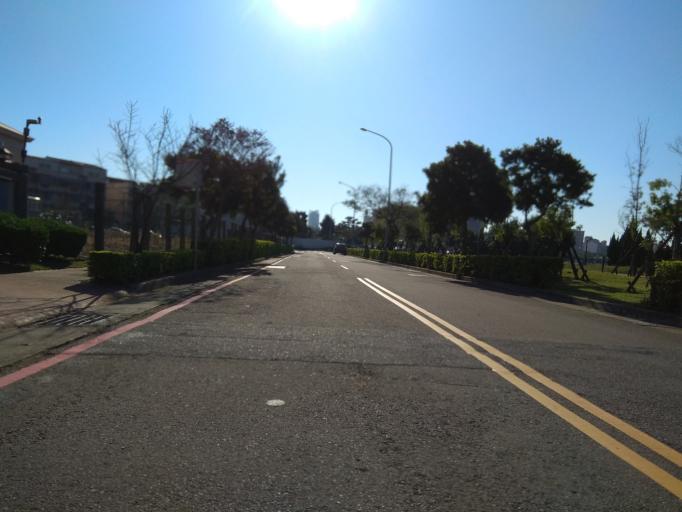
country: TW
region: Taiwan
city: Taoyuan City
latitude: 25.0200
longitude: 121.2180
